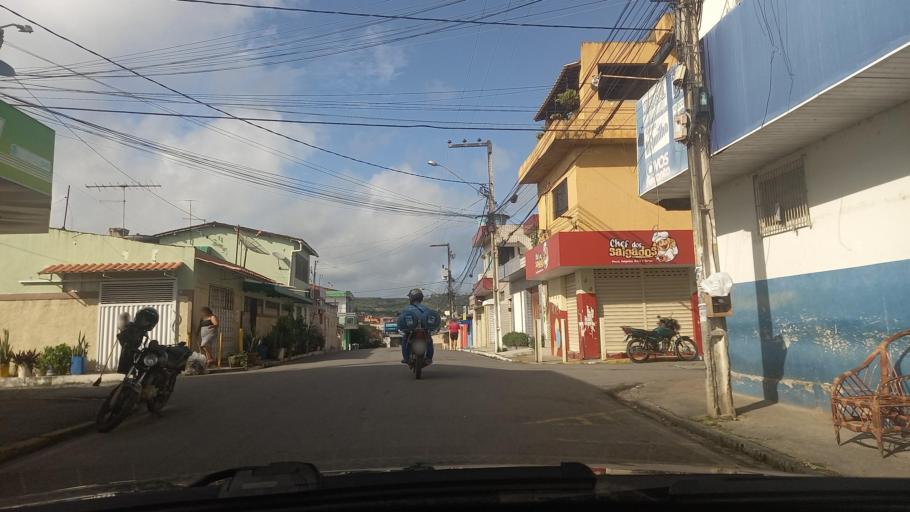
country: BR
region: Pernambuco
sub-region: Vitoria De Santo Antao
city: Vitoria de Santo Antao
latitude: -8.1177
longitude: -35.2788
